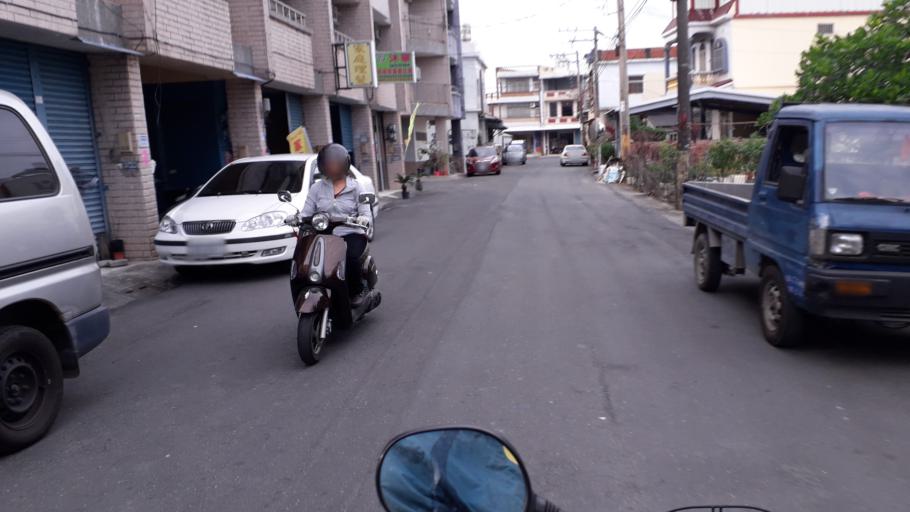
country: TW
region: Taiwan
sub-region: Pingtung
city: Pingtung
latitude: 22.3649
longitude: 120.6015
